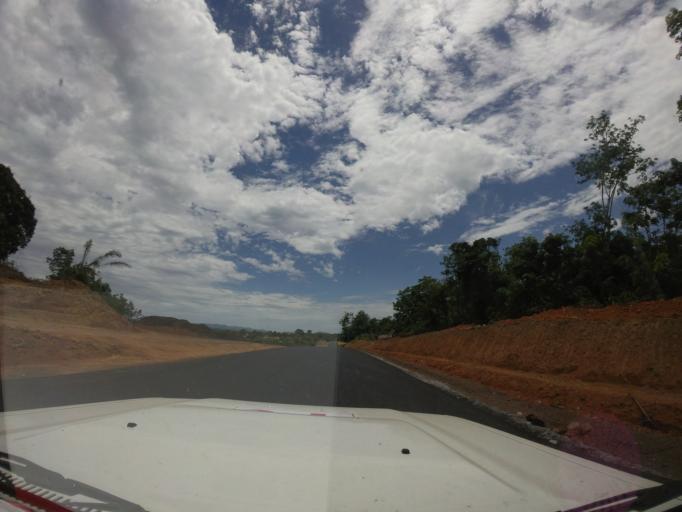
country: LR
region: Margibi
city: Kakata
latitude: 6.7241
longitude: -10.1525
